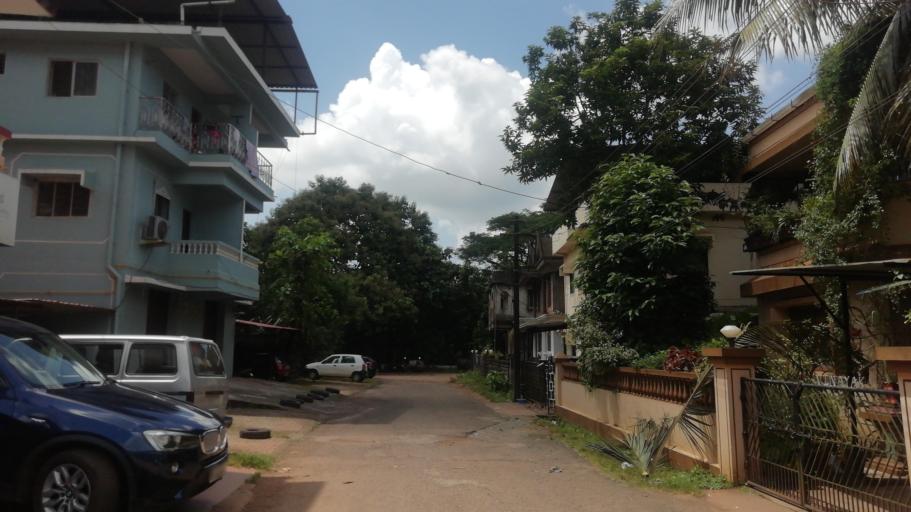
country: IN
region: Goa
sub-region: North Goa
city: Queula
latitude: 15.3853
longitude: 74.0032
